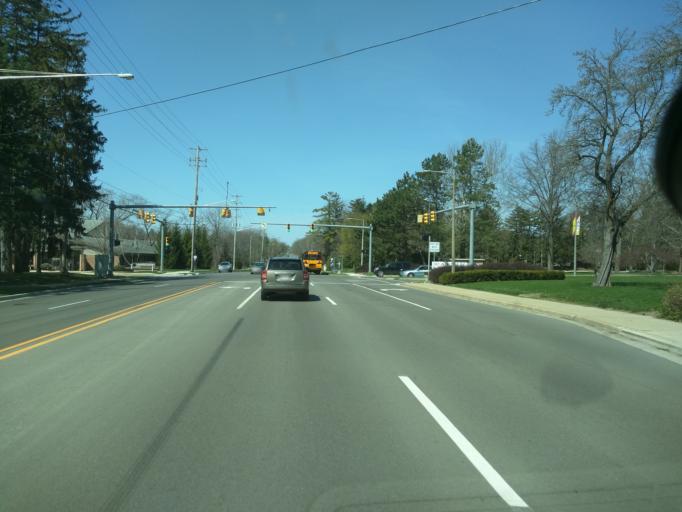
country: US
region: Michigan
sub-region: Kent County
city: East Grand Rapids
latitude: 42.9270
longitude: -85.5882
